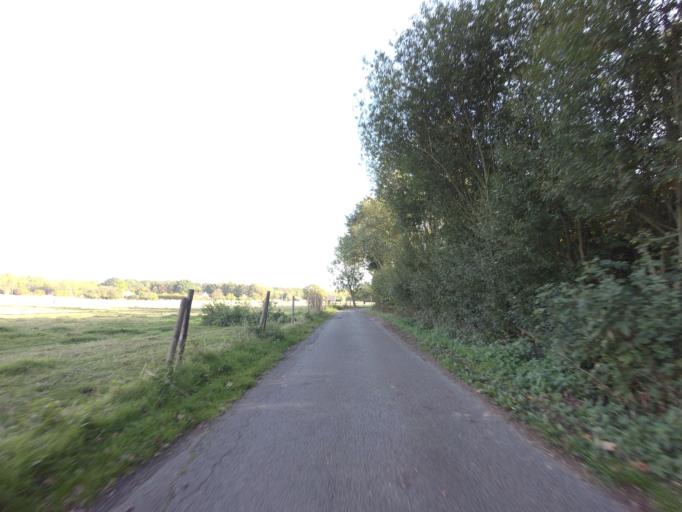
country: BE
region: Flanders
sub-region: Provincie Vlaams-Brabant
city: Kampenhout
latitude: 50.9220
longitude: 4.5952
